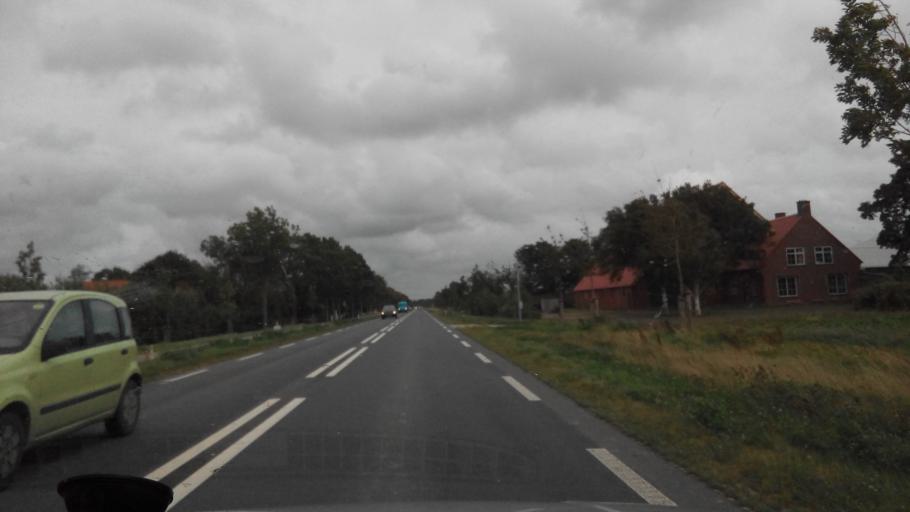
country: NL
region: North Holland
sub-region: Gemeente Hollands Kroon
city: Den Oever
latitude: 52.8444
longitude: 4.9890
